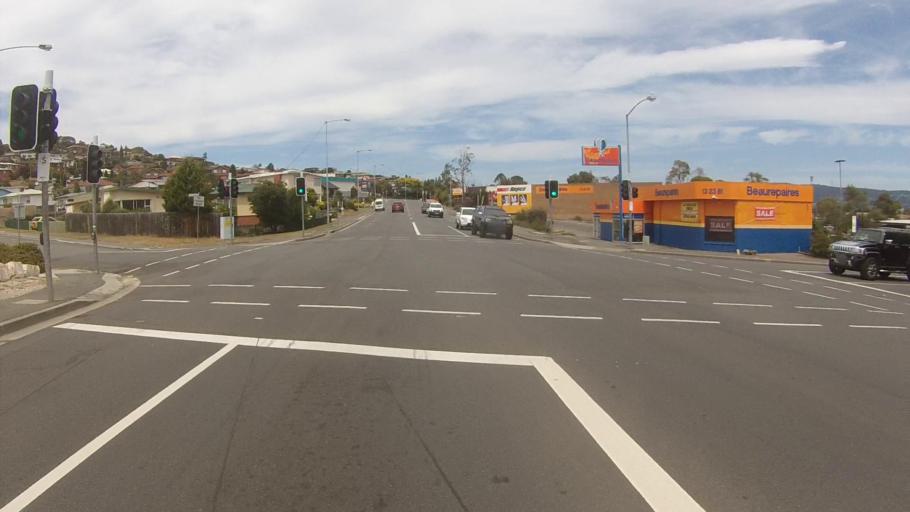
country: AU
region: Tasmania
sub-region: Clarence
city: Bellerive
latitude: -42.8646
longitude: 147.3720
